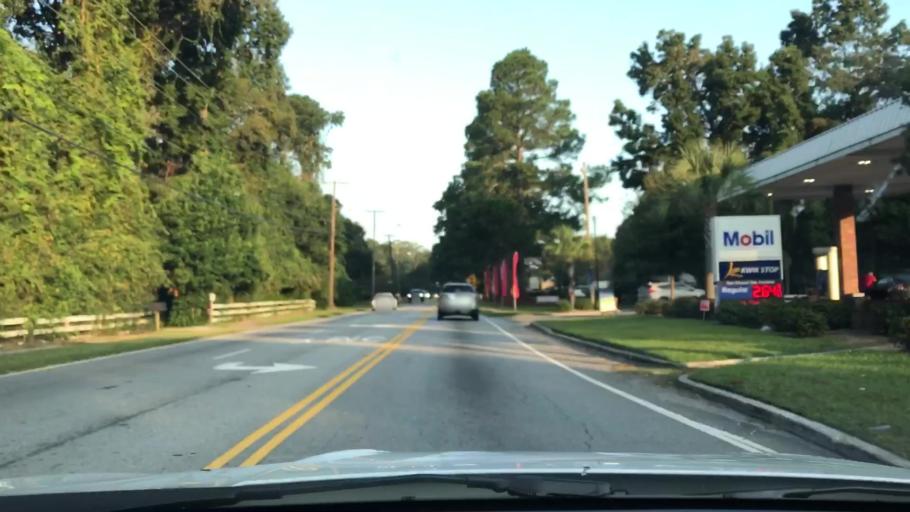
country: US
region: South Carolina
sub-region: Charleston County
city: North Charleston
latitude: 32.8095
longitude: -80.0259
